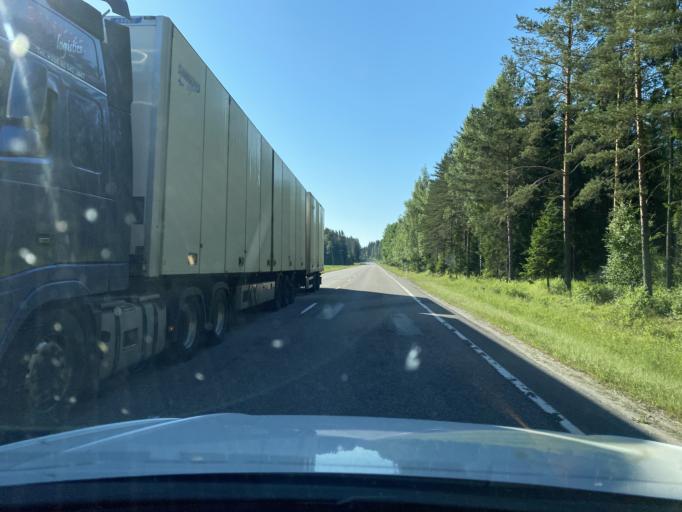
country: FI
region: Haeme
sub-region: Haemeenlinna
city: Renko
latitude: 60.7572
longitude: 24.2973
